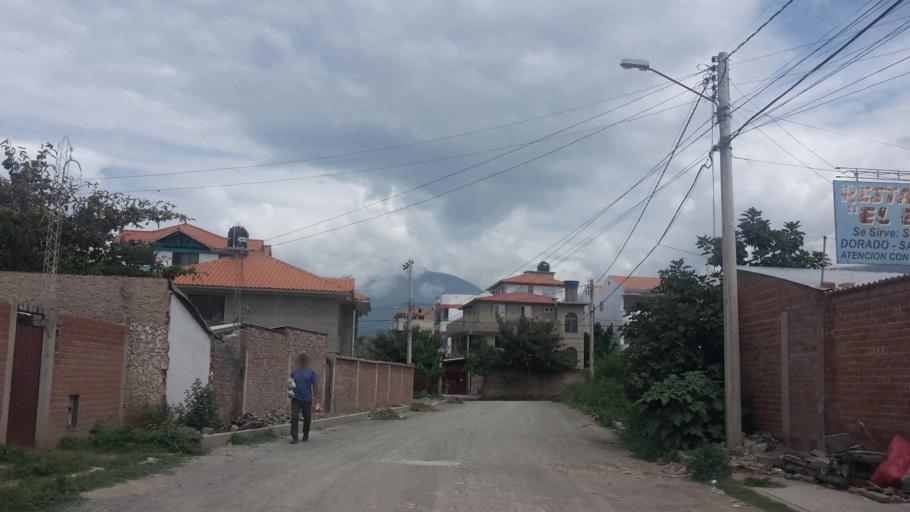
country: BO
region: Cochabamba
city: Cochabamba
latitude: -17.3365
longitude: -66.2162
